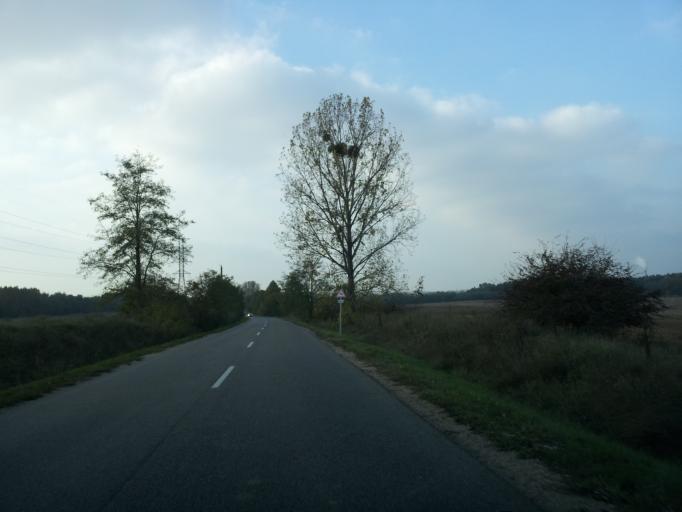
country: HU
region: Komarom-Esztergom
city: Oroszlany
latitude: 47.4773
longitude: 18.2854
